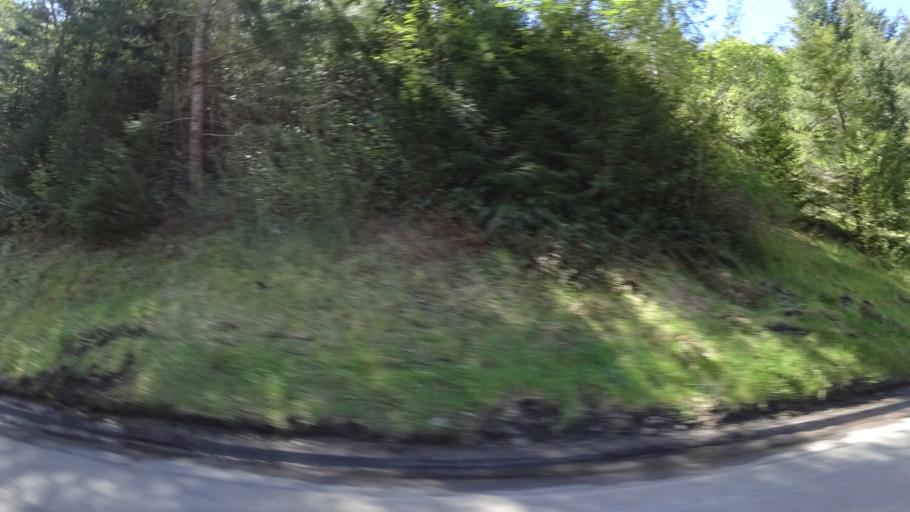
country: US
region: California
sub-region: Del Norte County
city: Bertsch-Oceanview
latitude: 41.4280
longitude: -124.0134
